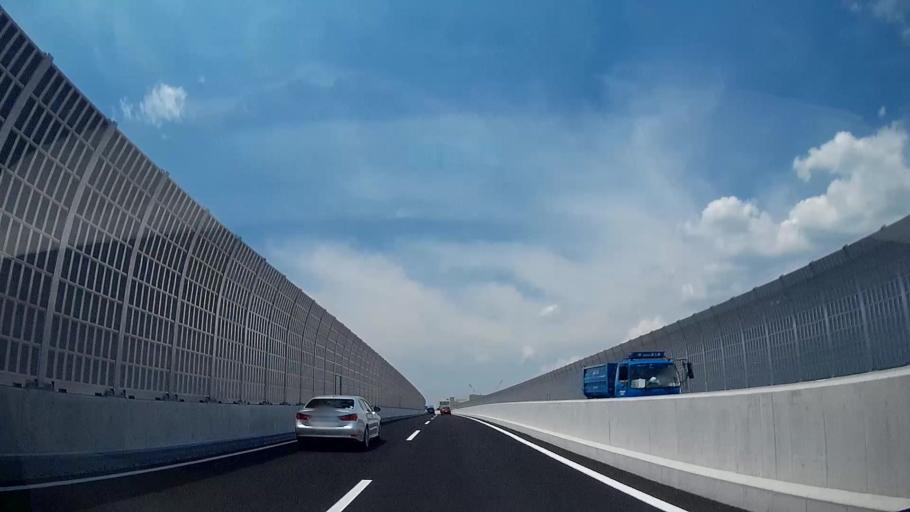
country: JP
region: Tokyo
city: Urayasu
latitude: 35.7067
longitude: 139.9263
